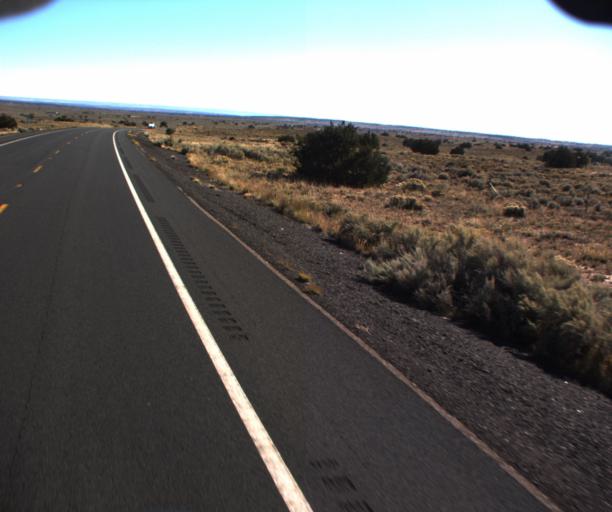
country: US
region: Arizona
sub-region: Apache County
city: Houck
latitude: 35.3196
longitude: -109.4322
